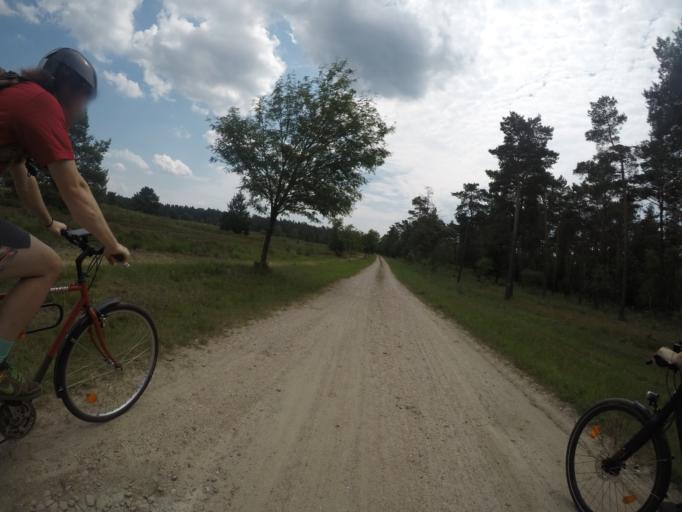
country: DE
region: Lower Saxony
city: Asendorf
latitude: 53.2485
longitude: 9.9562
